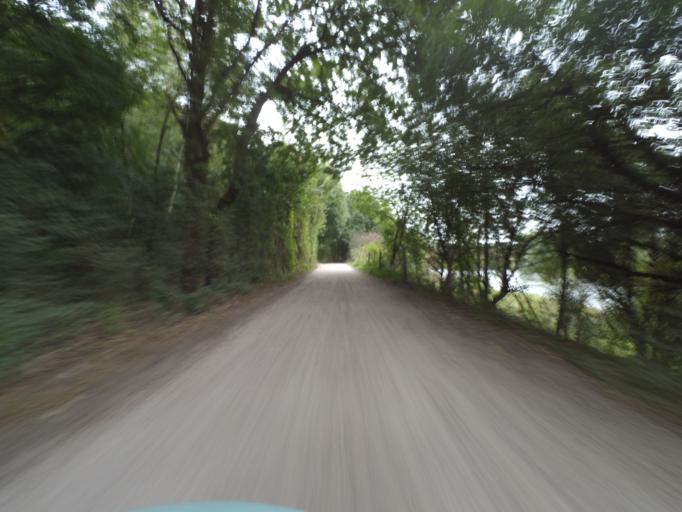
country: NL
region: Utrecht
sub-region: Gemeente Rhenen
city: Rhenen
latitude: 51.9506
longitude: 5.6007
